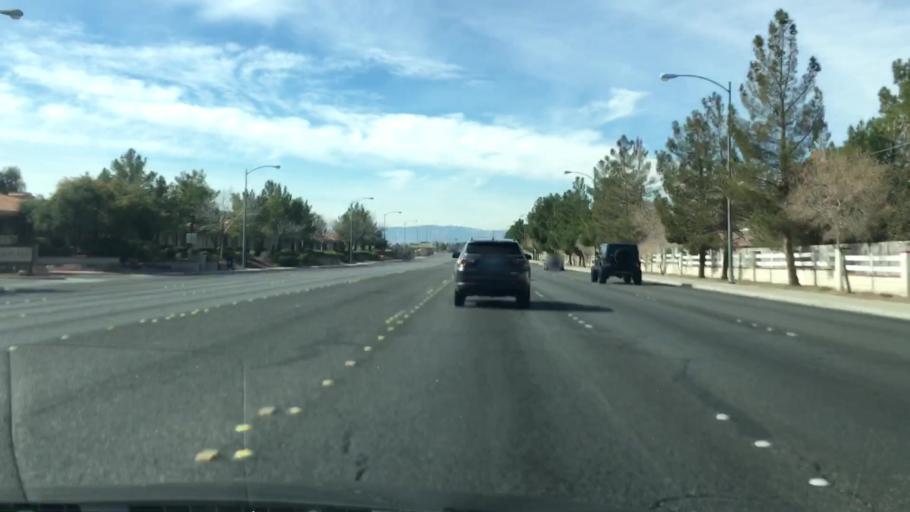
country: US
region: Nevada
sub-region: Clark County
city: Whitney
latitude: 36.0571
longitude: -115.1074
